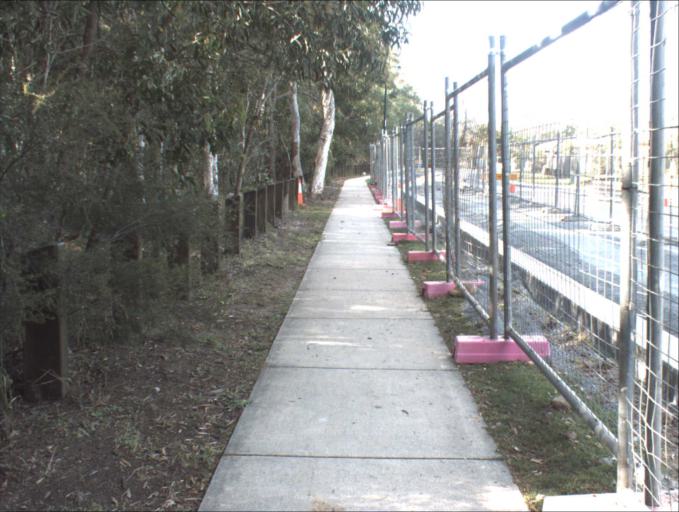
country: AU
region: Queensland
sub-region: Logan
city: Park Ridge South
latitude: -27.6853
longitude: 153.0517
